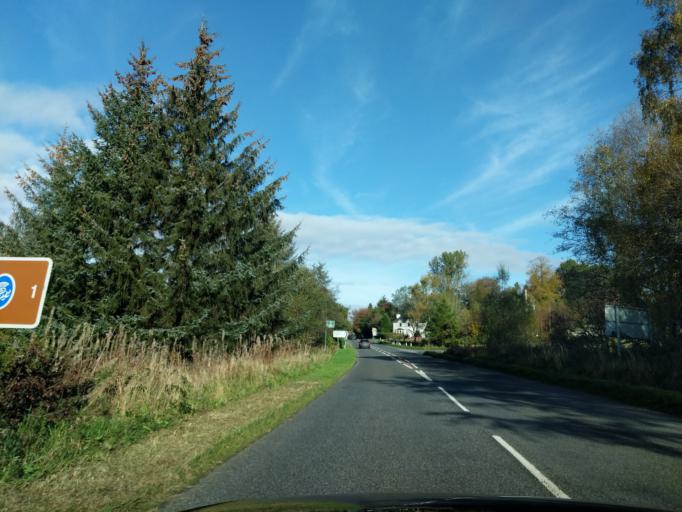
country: GB
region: Scotland
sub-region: Dumfries and Galloway
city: Castle Douglas
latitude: 55.0794
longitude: -4.1297
